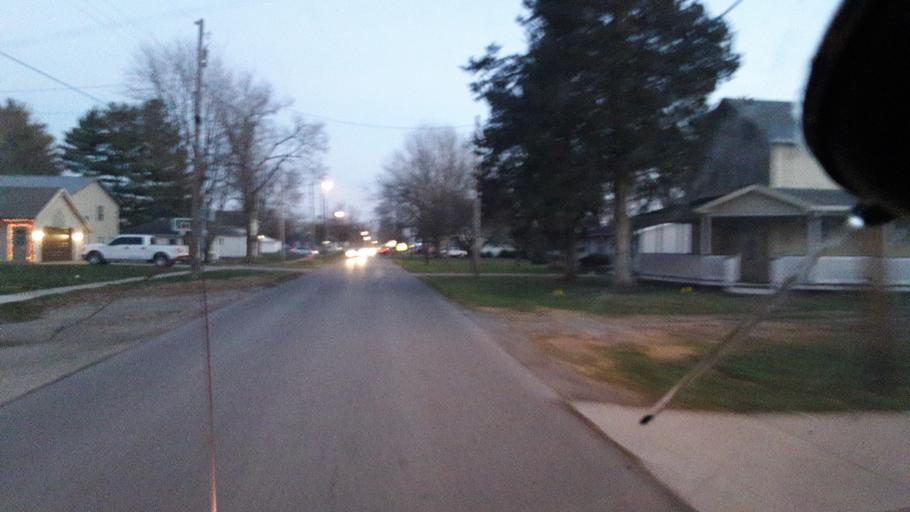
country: US
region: Ohio
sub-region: Defiance County
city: Hicksville
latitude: 41.2934
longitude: -84.7721
